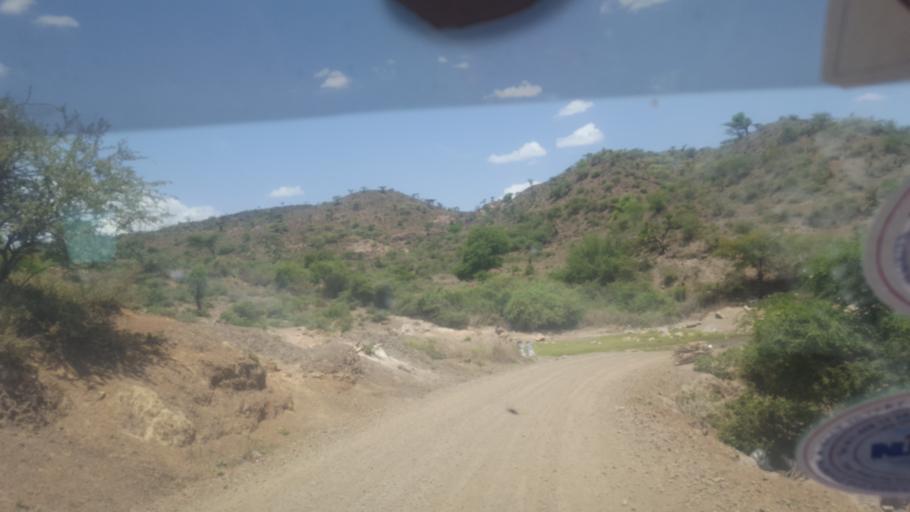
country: ET
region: Oromiya
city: Deder
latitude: 9.5435
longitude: 41.4760
